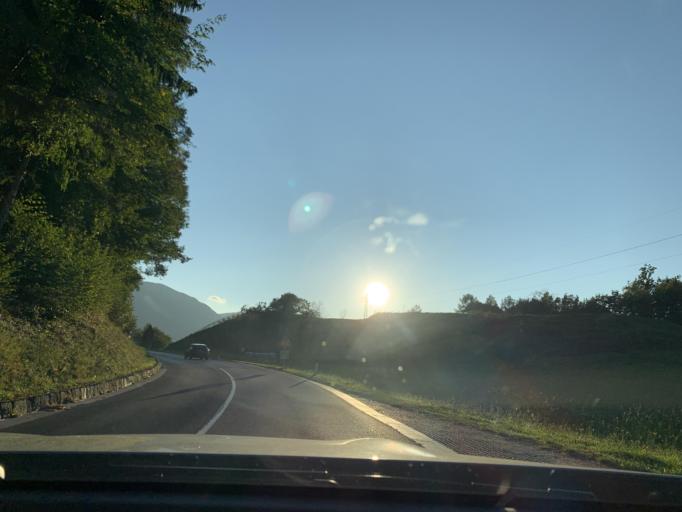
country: IT
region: Trentino-Alto Adige
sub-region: Bolzano
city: Fie Allo Sciliar
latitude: 46.5039
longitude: 11.4734
